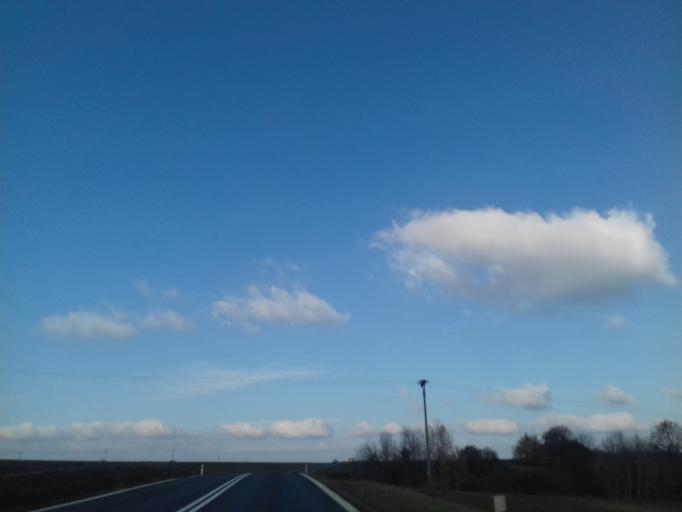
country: CZ
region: Plzensky
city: Stankov
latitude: 49.5760
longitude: 13.0797
